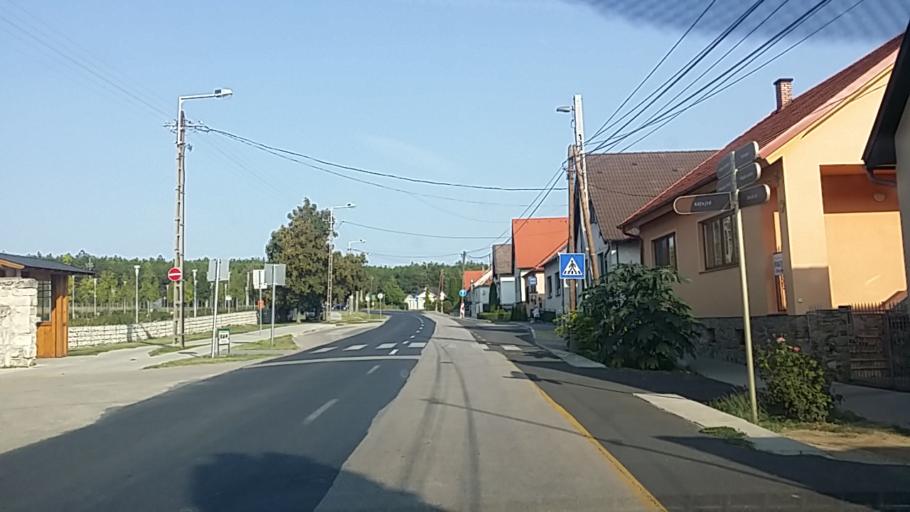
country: HU
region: Gyor-Moson-Sopron
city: Fertorakos
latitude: 47.7267
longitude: 16.6448
